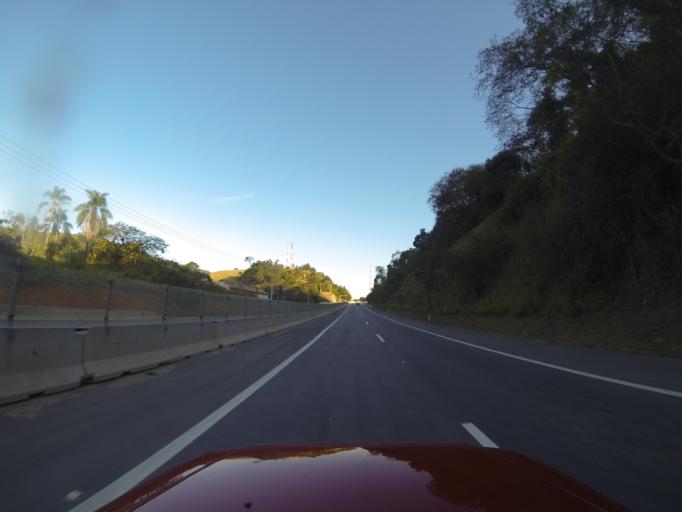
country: BR
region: Sao Paulo
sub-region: Santa Branca
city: Santa Branca
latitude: -23.3793
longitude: -45.6638
